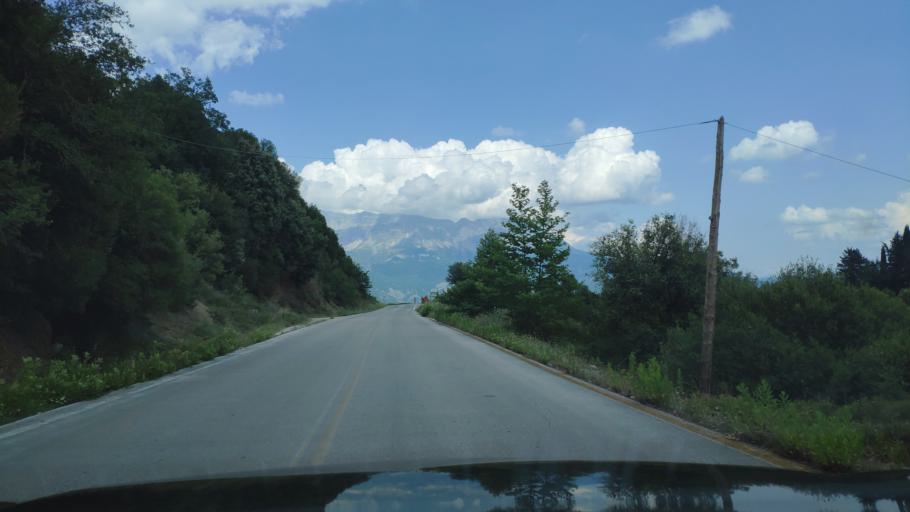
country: GR
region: Epirus
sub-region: Nomos Artas
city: Agios Dimitrios
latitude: 39.3571
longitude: 21.0200
